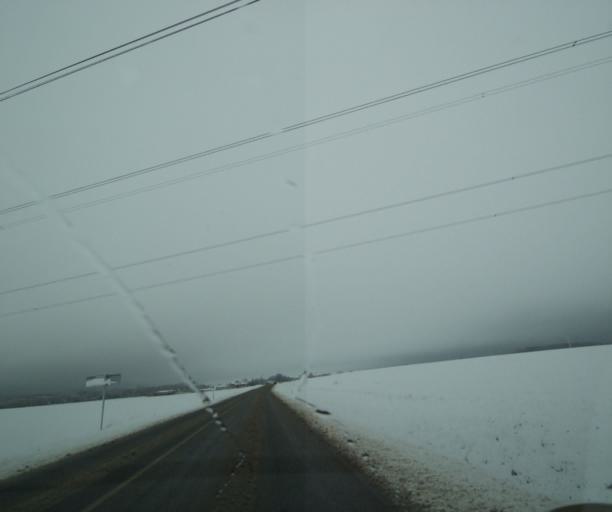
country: FR
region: Champagne-Ardenne
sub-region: Departement de la Haute-Marne
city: Wassy
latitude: 48.5180
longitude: 4.9348
